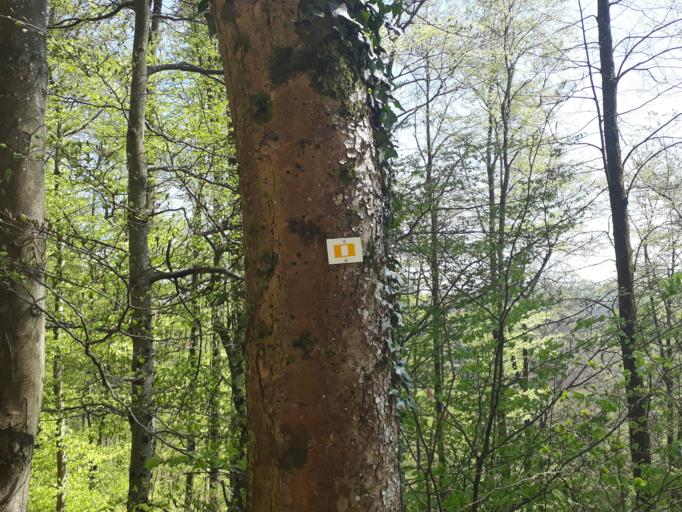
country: FR
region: Lorraine
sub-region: Departement de la Moselle
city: Phalsbourg
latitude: 48.8556
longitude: 7.2976
